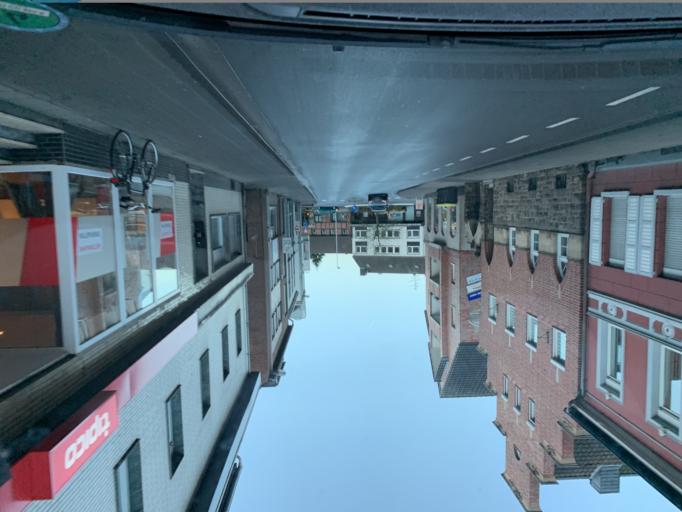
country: DE
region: North Rhine-Westphalia
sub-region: Regierungsbezirk Dusseldorf
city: Juchen
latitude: 51.1013
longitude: 6.5031
